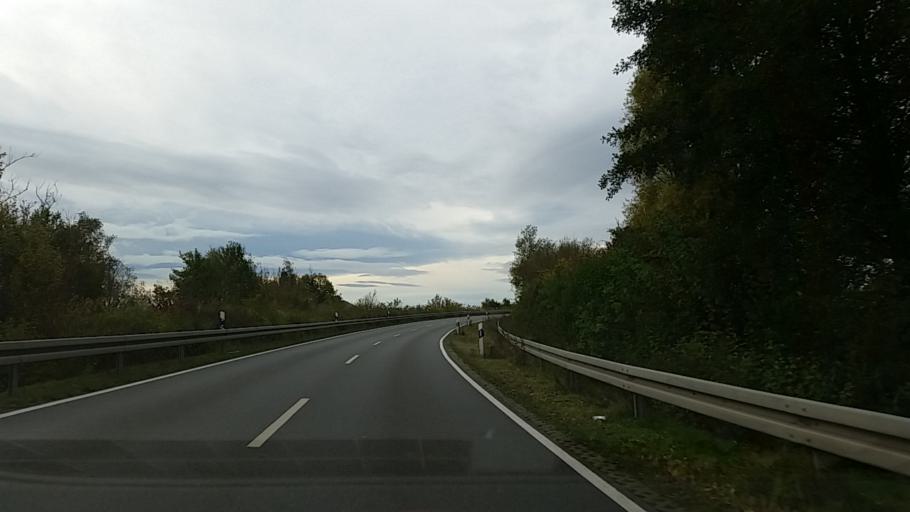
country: DE
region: Lower Saxony
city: Isenbuttel
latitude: 52.4457
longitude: 10.5857
